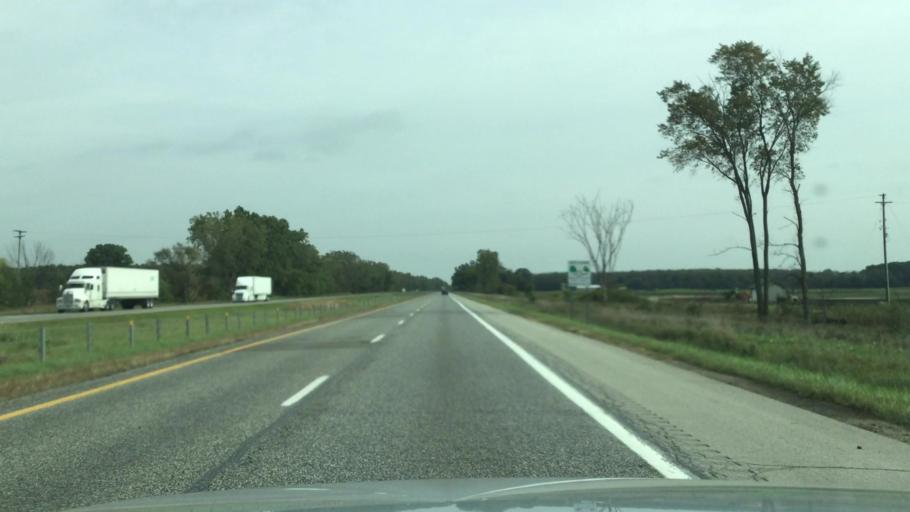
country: US
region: Michigan
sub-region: Shiawassee County
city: Corunna
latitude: 42.8786
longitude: -84.1225
